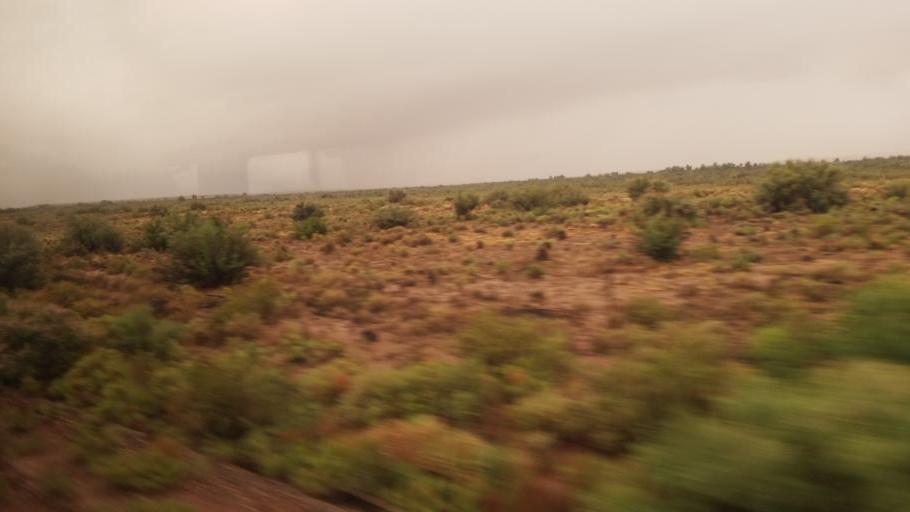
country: US
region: Arizona
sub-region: Navajo County
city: Joseph City
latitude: 34.9674
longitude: -110.4474
